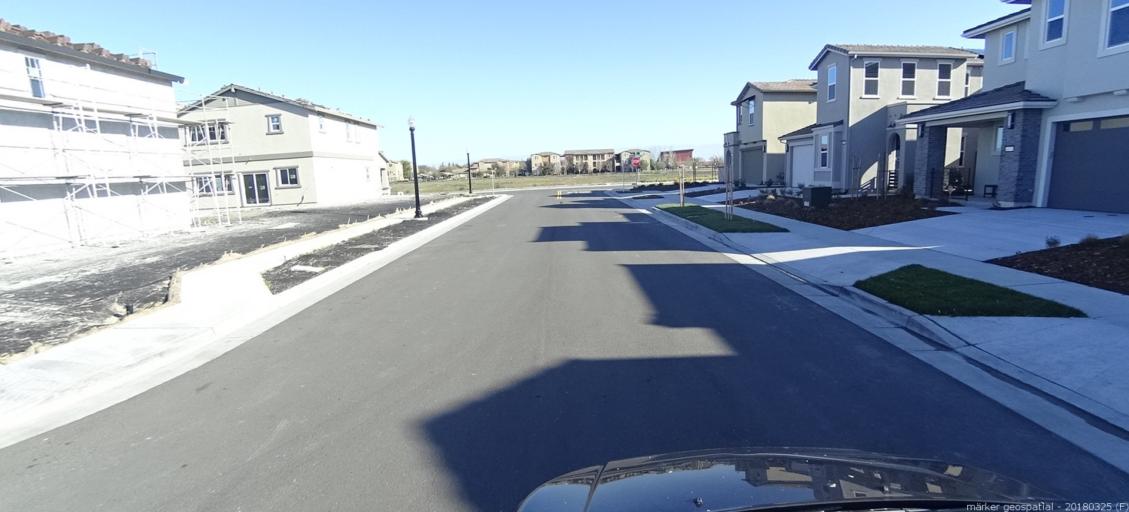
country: US
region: California
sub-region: Sacramento County
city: Rio Linda
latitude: 38.6527
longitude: -121.4957
